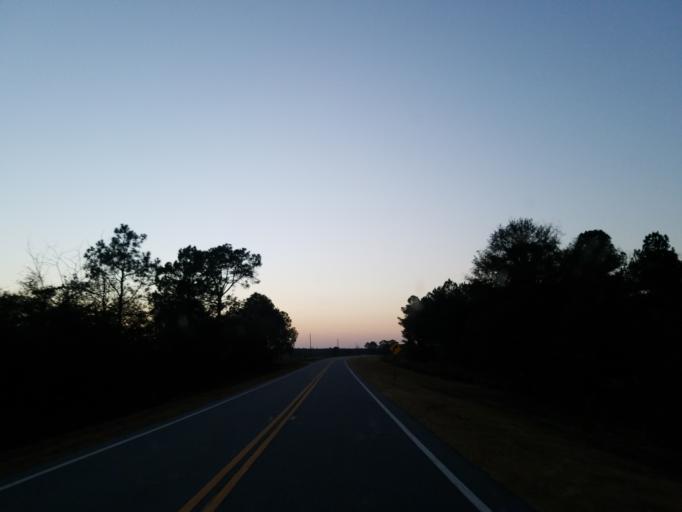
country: US
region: Georgia
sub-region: Wilcox County
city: Rochelle
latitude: 31.8159
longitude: -83.5267
